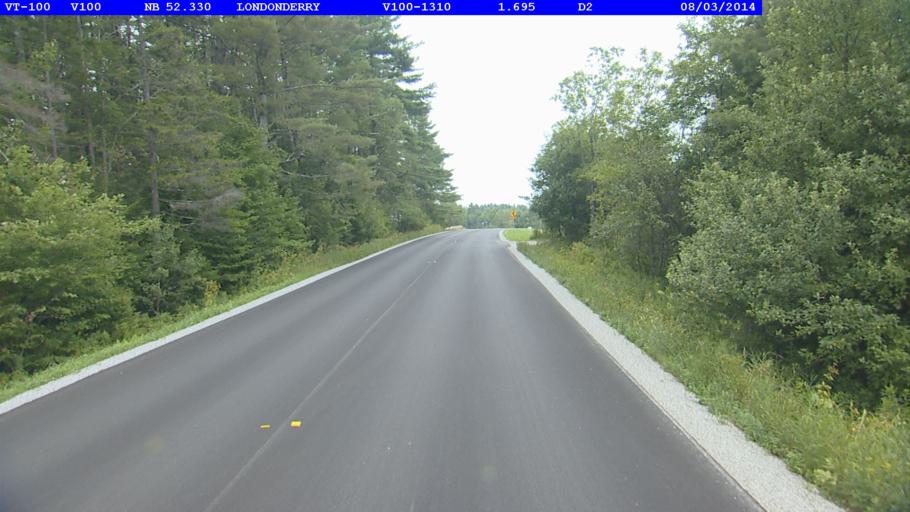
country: US
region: Vermont
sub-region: Windham County
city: Dover
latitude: 43.1757
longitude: -72.8204
